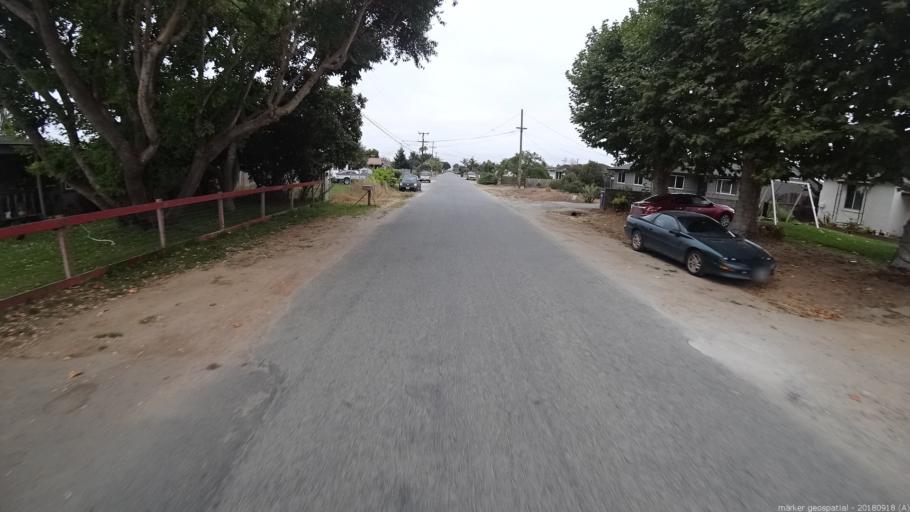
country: US
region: California
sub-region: Monterey County
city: Prunedale
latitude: 36.7548
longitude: -121.6167
